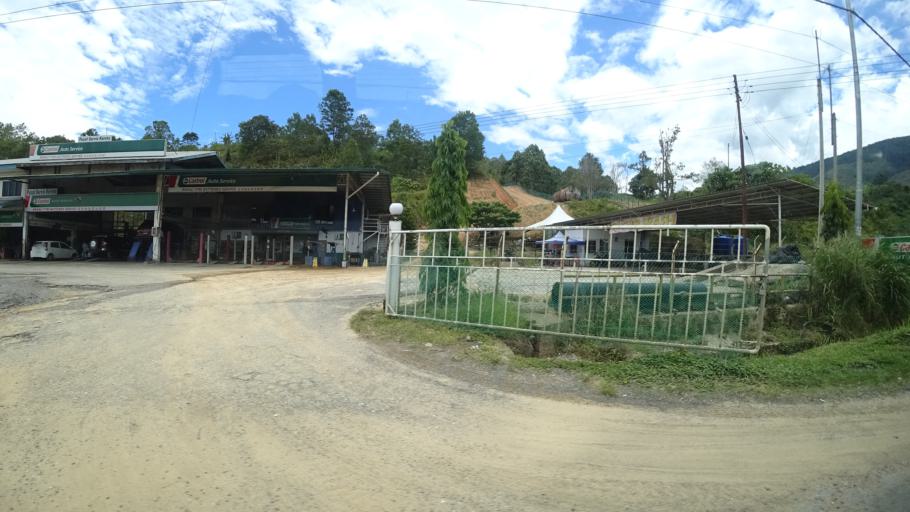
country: MY
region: Sabah
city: Ranau
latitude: 5.9740
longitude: 116.6797
